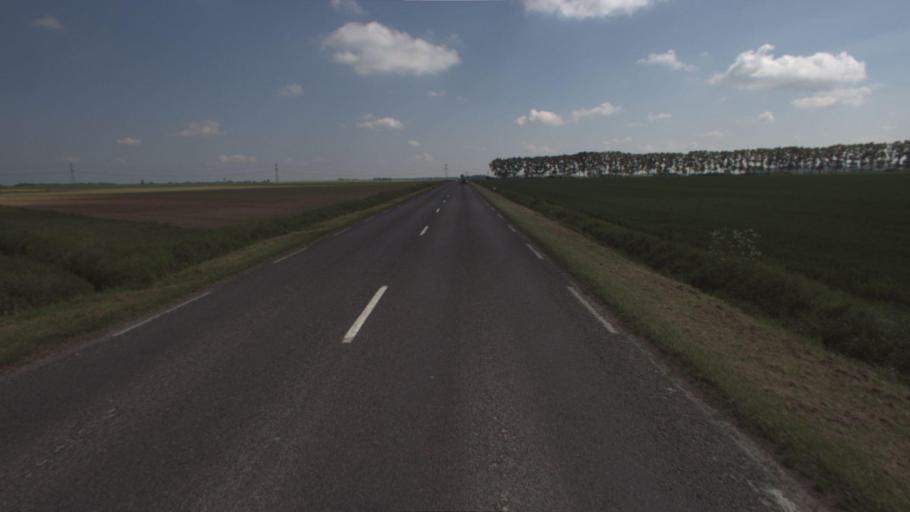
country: FR
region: Ile-de-France
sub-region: Departement de Seine-et-Marne
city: Ozouer-le-Voulgis
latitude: 48.6188
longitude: 2.7557
